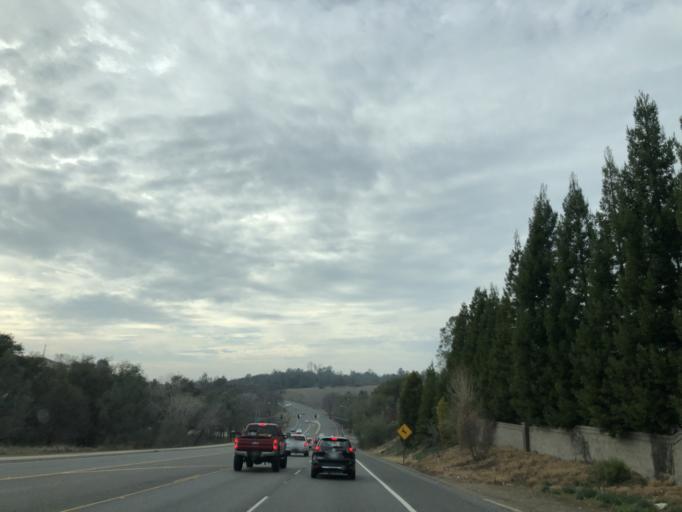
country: US
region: California
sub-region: El Dorado County
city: El Dorado Hills
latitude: 38.7092
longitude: -121.0896
